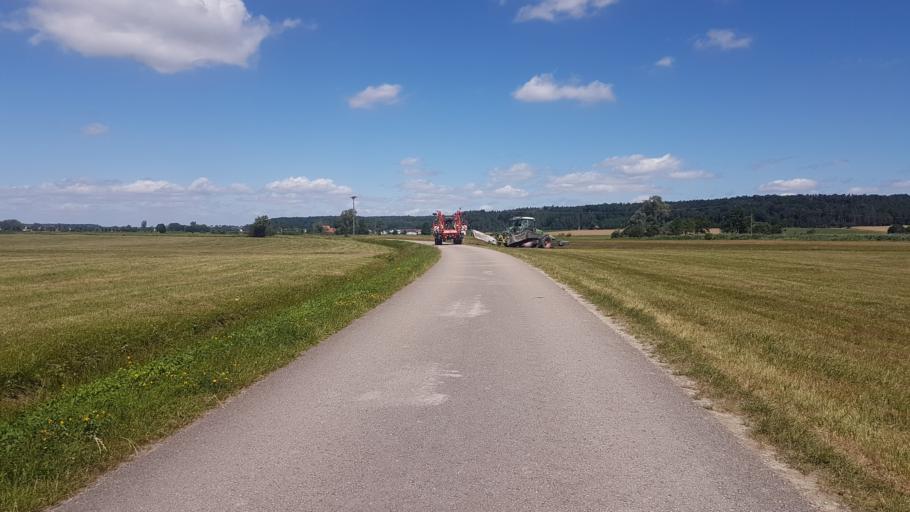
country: DE
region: Bavaria
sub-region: Regierungsbezirk Mittelfranken
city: Aurach
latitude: 49.2663
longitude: 10.4455
